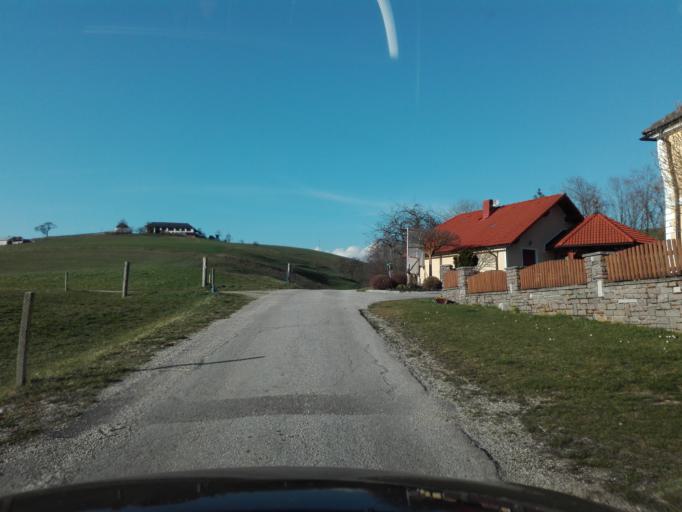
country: AT
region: Upper Austria
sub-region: Politischer Bezirk Perg
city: Bad Kreuzen
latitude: 48.2482
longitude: 14.7450
